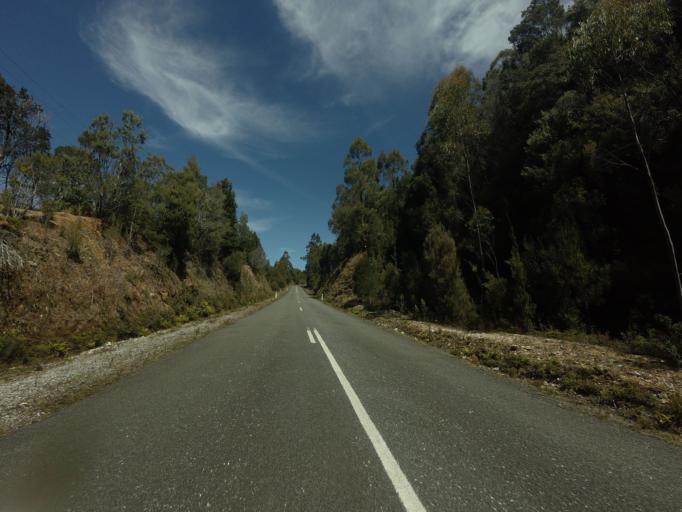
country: AU
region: Tasmania
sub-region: West Coast
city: Queenstown
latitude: -42.7778
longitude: 146.0366
